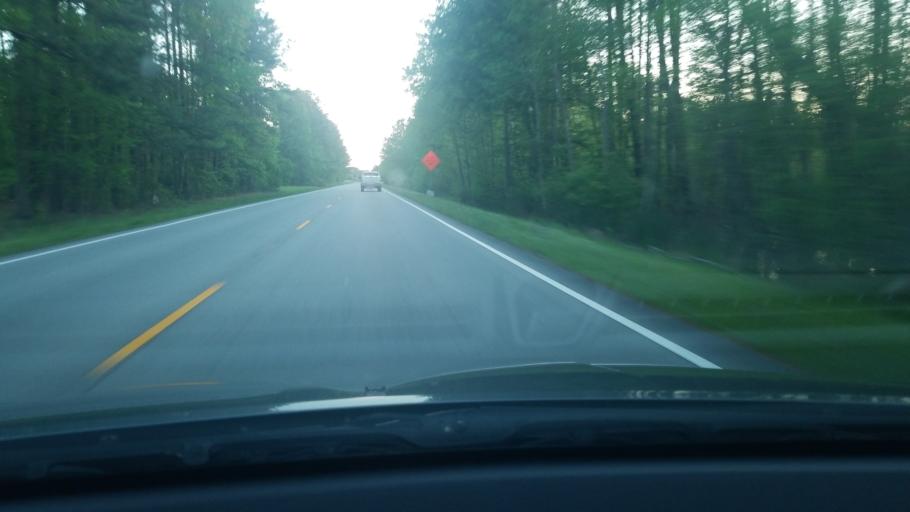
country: US
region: North Carolina
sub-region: Craven County
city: Vanceboro
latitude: 35.2435
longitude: -77.0958
